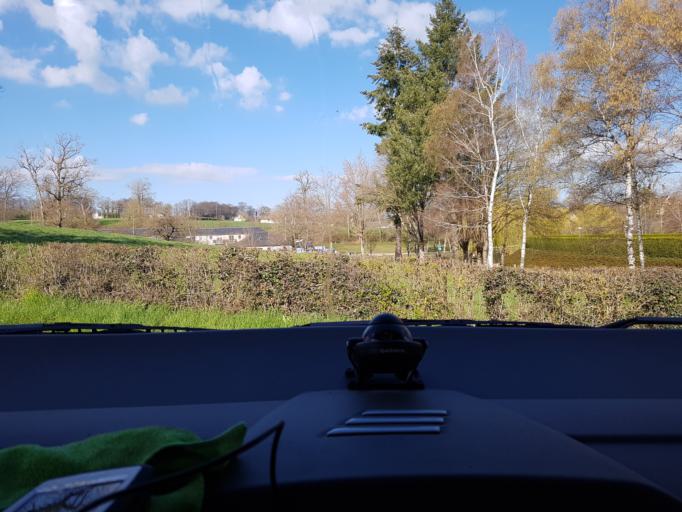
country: FR
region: Midi-Pyrenees
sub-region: Departement de l'Aveyron
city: Colombies
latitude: 44.4045
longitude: 2.2894
